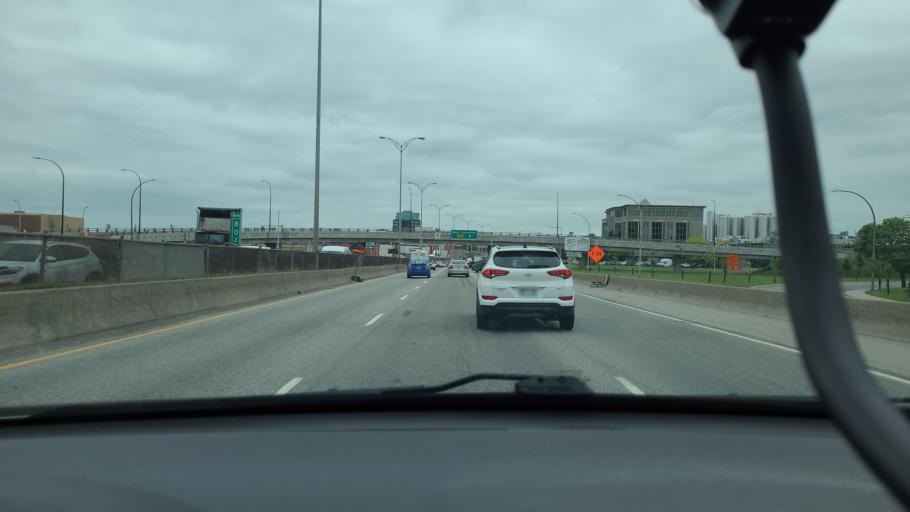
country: CA
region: Quebec
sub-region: Montreal
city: Saint-Leonard
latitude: 45.5976
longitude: -73.5715
